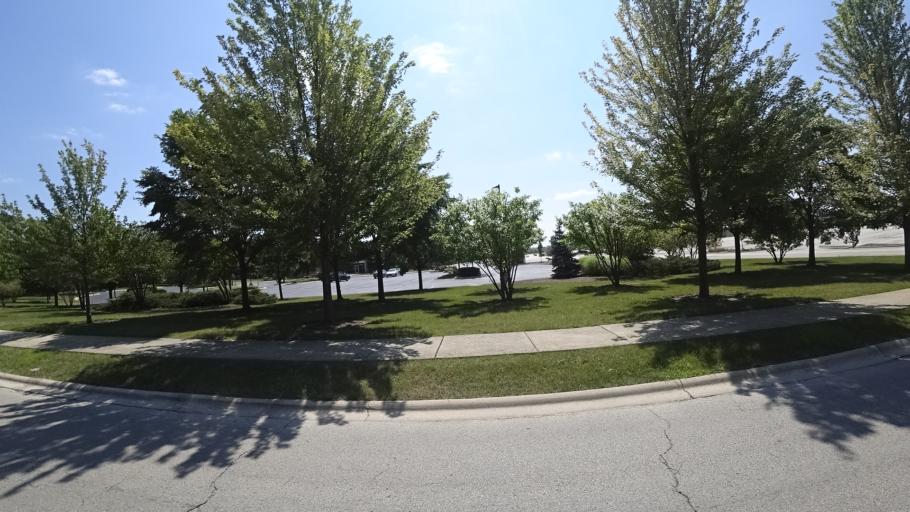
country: US
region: Illinois
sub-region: Cook County
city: Orland Park
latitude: 41.6226
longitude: -87.8453
